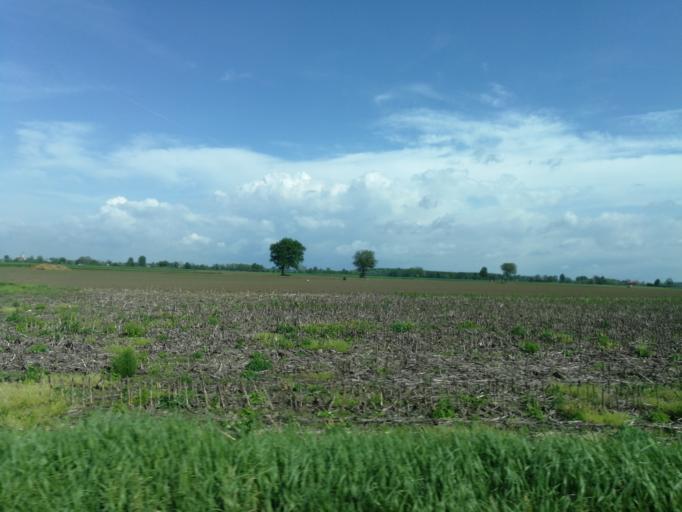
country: IT
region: Piedmont
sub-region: Provincia di Cuneo
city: Faule
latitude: 44.7961
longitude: 7.5747
